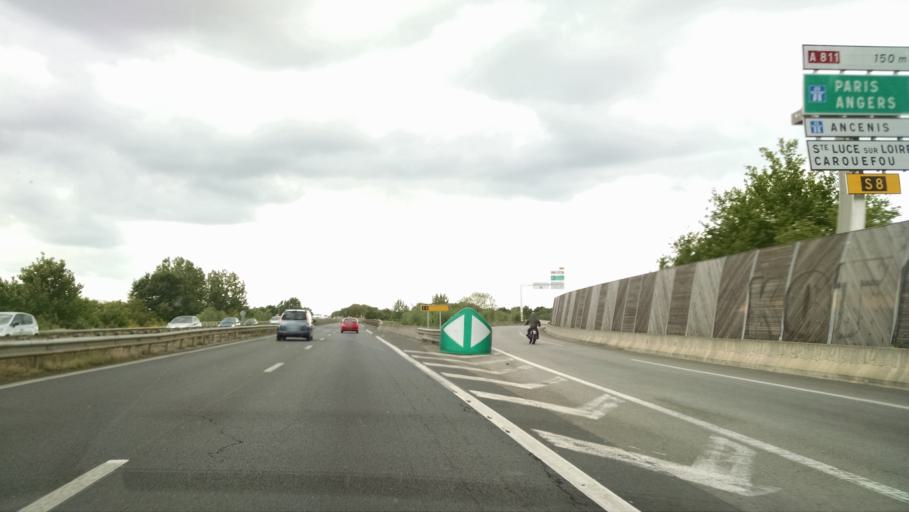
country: FR
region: Pays de la Loire
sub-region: Departement de la Loire-Atlantique
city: Sainte-Luce-sur-Loire
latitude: 47.2343
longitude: -1.4765
